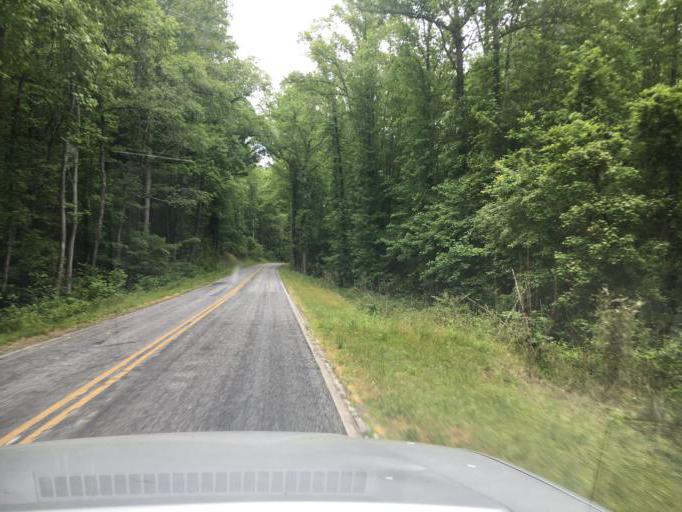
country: US
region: South Carolina
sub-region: Greenville County
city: Tigerville
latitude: 35.1345
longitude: -82.4073
